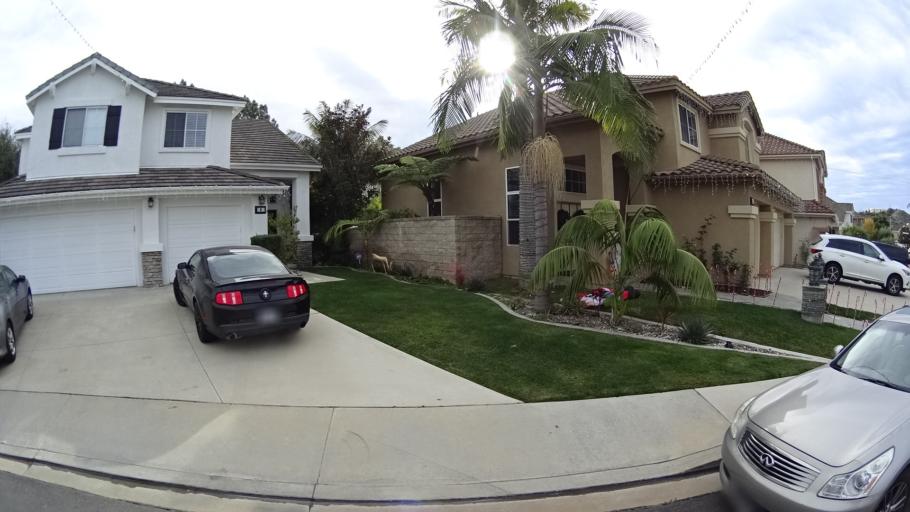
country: US
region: California
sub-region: Orange County
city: Aliso Viejo
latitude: 33.5835
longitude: -117.7409
